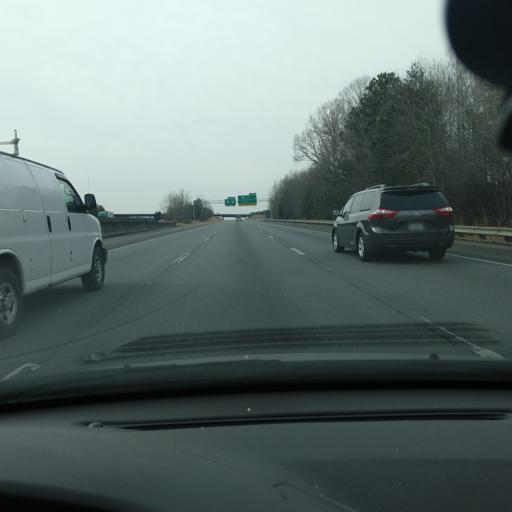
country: US
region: North Carolina
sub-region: Gaston County
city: Bessemer City
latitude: 35.2541
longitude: -81.2944
